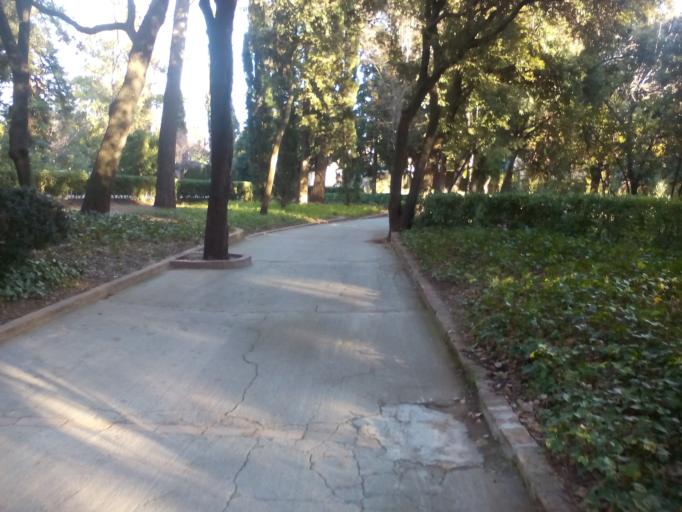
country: ES
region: Catalonia
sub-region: Provincia de Barcelona
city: Horta-Guinardo
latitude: 41.4399
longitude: 2.1456
